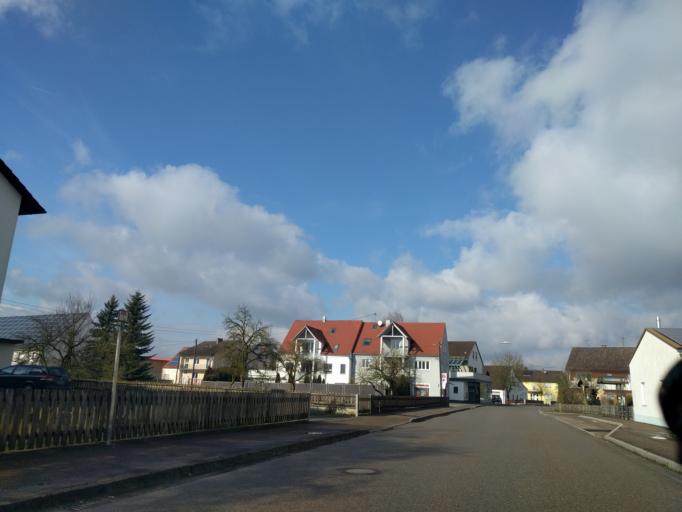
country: DE
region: Bavaria
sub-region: Swabia
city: Genderkingen
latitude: 48.7039
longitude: 10.8790
